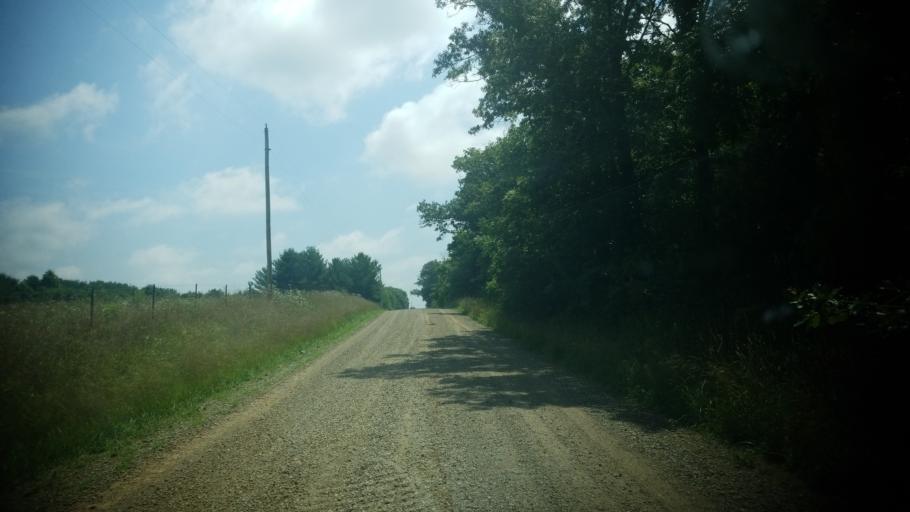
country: US
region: Illinois
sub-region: Wayne County
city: Fairfield
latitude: 38.5300
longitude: -88.3950
